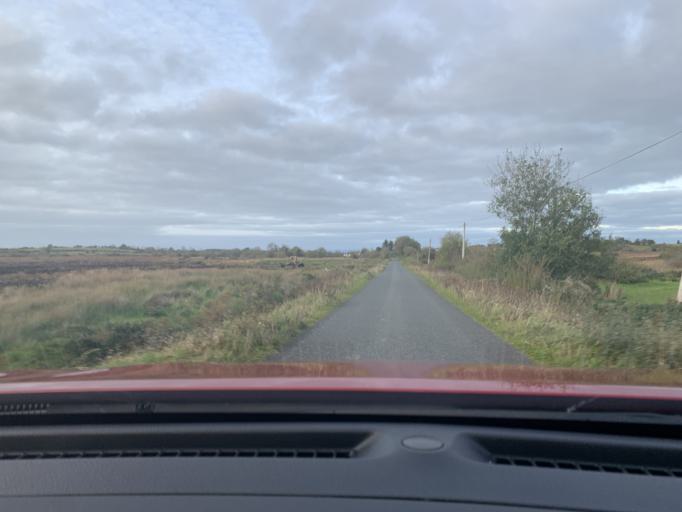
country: IE
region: Connaught
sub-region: Roscommon
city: Ballaghaderreen
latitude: 53.9943
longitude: -8.6090
